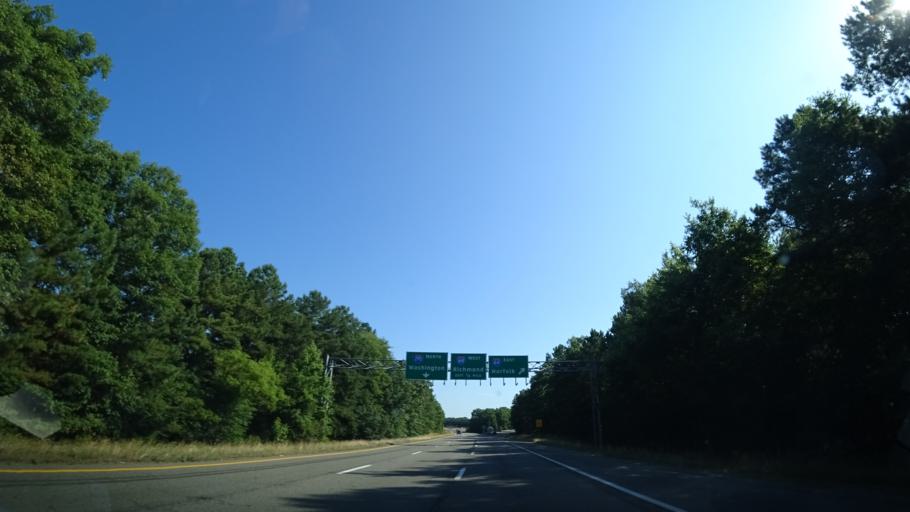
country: US
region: Virginia
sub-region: Henrico County
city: Sandston
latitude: 37.5149
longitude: -77.2707
